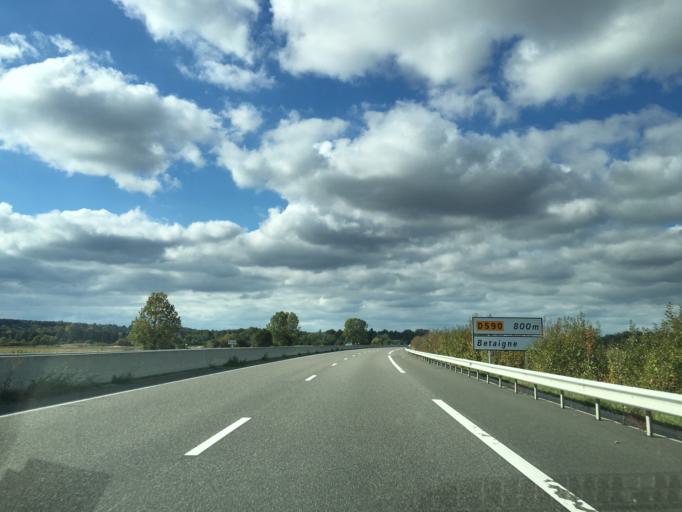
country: FR
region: Lorraine
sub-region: Departement de Meurthe-et-Moselle
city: Gerbeviller
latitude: 48.5309
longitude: 6.5867
